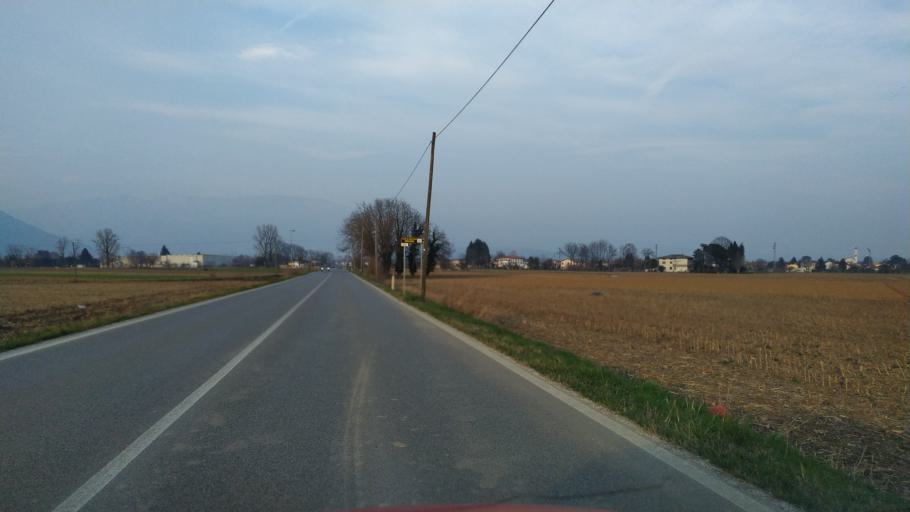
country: IT
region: Veneto
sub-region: Provincia di Vicenza
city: Giavenale
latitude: 45.6878
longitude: 11.4128
